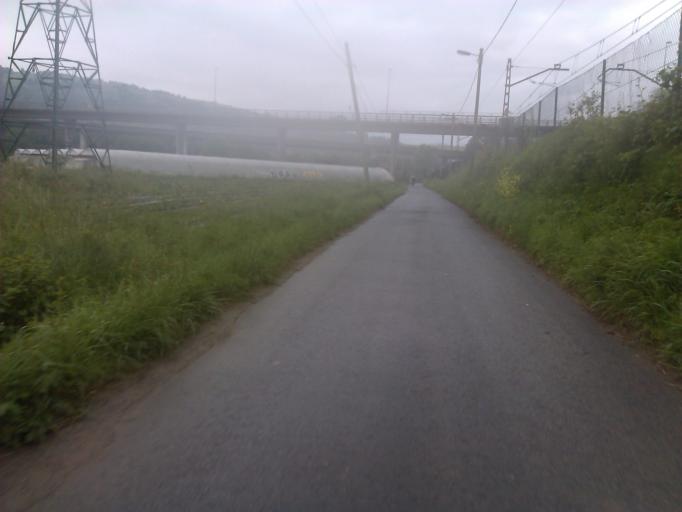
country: ES
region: Basque Country
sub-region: Provincia de Guipuzcoa
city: Astigarraga
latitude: 43.2898
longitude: -1.9556
